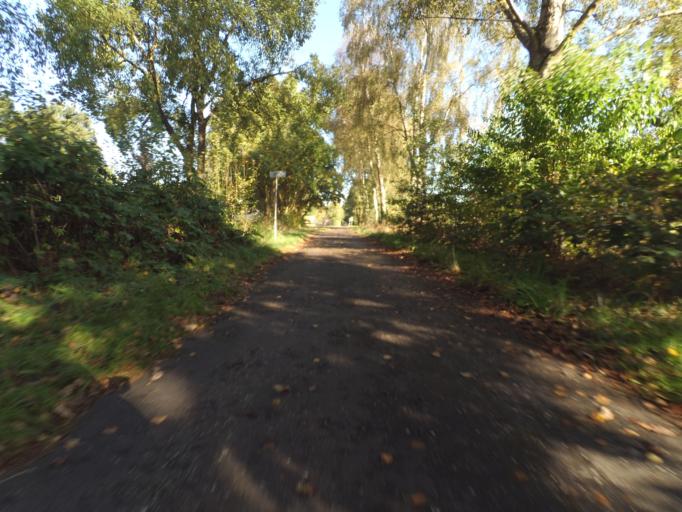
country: NL
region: Gelderland
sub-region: Gemeente Epe
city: Vaassen
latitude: 52.2547
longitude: 5.9661
